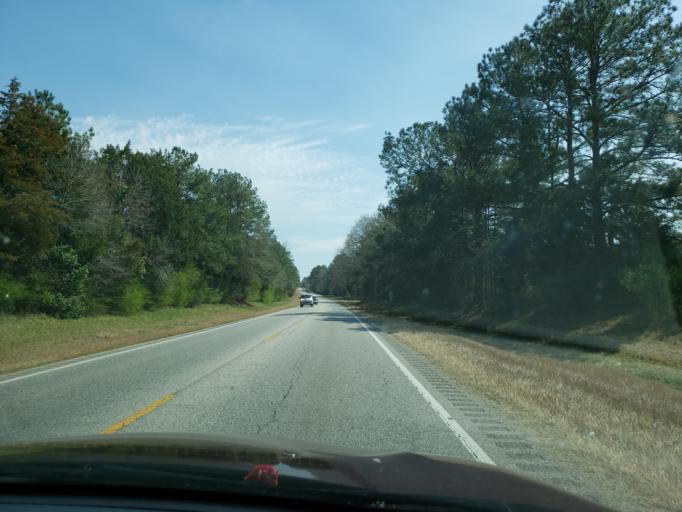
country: US
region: Alabama
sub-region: Elmore County
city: Elmore
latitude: 32.5444
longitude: -86.2756
